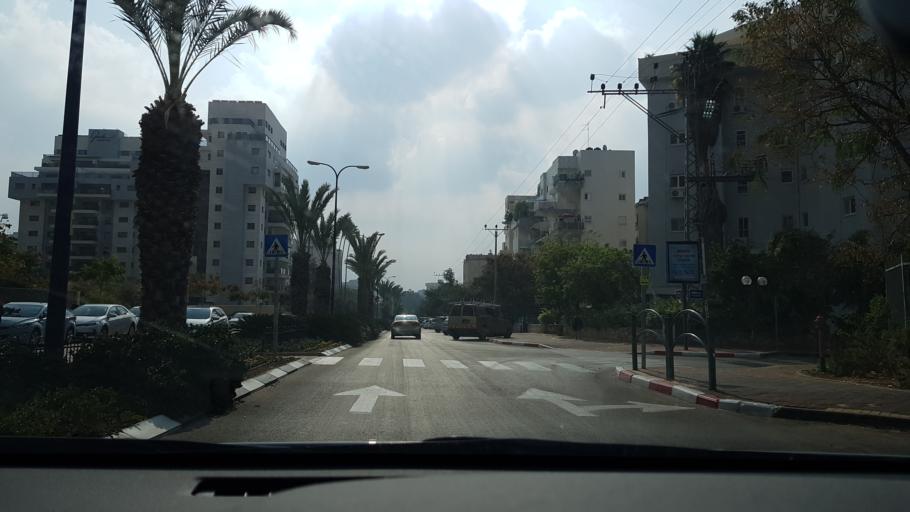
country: IL
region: Central District
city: Ness Ziona
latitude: 31.9024
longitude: 34.8191
